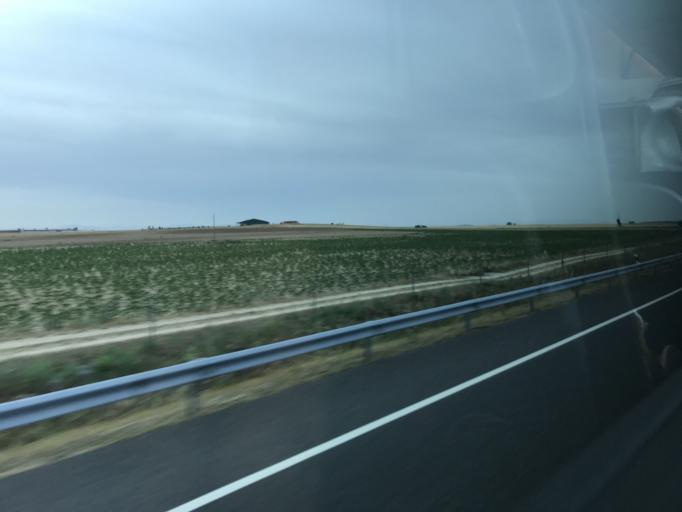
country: ES
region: Castille and Leon
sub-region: Provincia de Segovia
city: San Cristobal de la Vega
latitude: 41.1014
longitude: -4.6395
